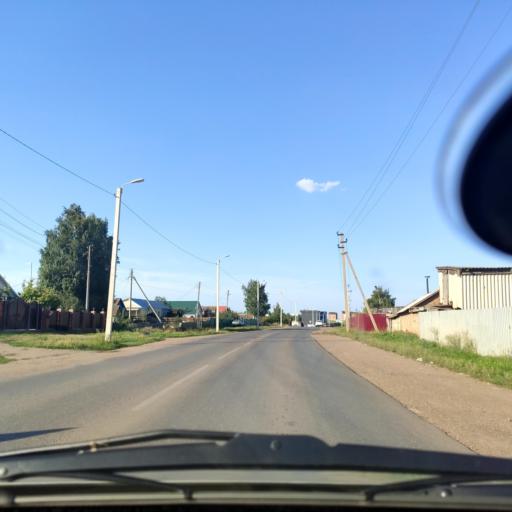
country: RU
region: Bashkortostan
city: Meleuz
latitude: 52.9601
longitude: 55.9067
